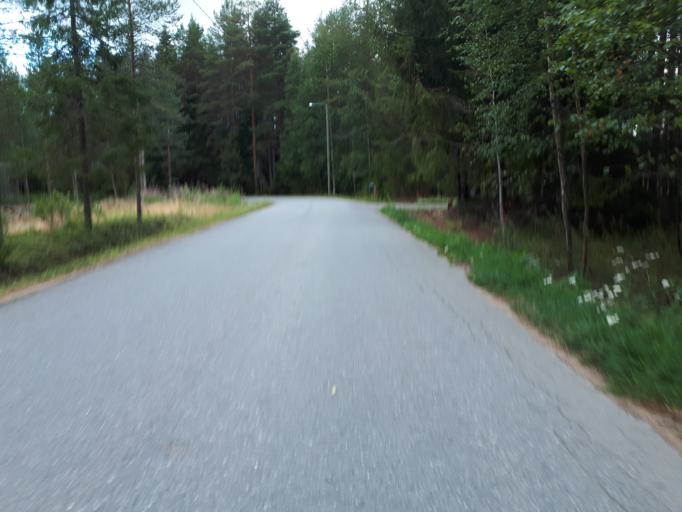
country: FI
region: Northern Ostrobothnia
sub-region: Oulunkaari
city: Ii
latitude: 65.3280
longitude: 25.3925
